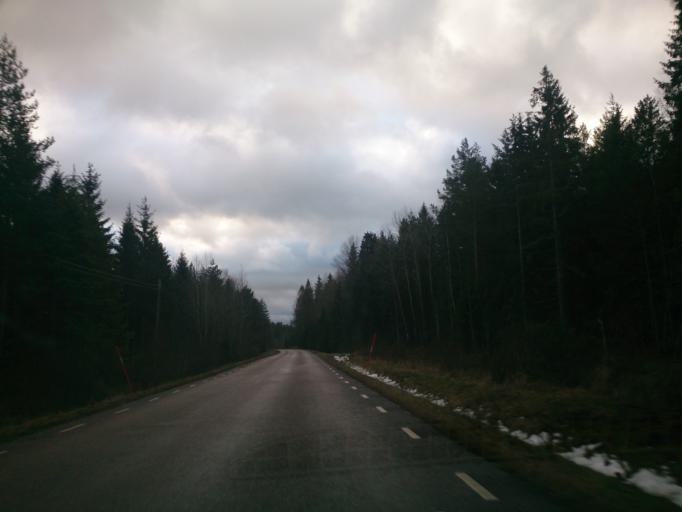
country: SE
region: OEstergoetland
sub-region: Atvidabergs Kommun
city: Atvidaberg
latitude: 58.3227
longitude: 16.0265
